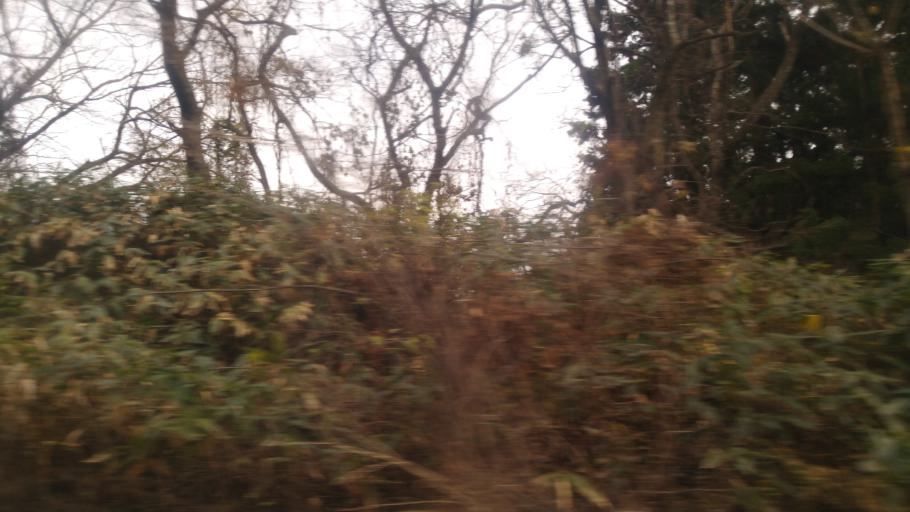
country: JP
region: Nagano
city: Nagano-shi
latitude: 36.4932
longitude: 138.1014
